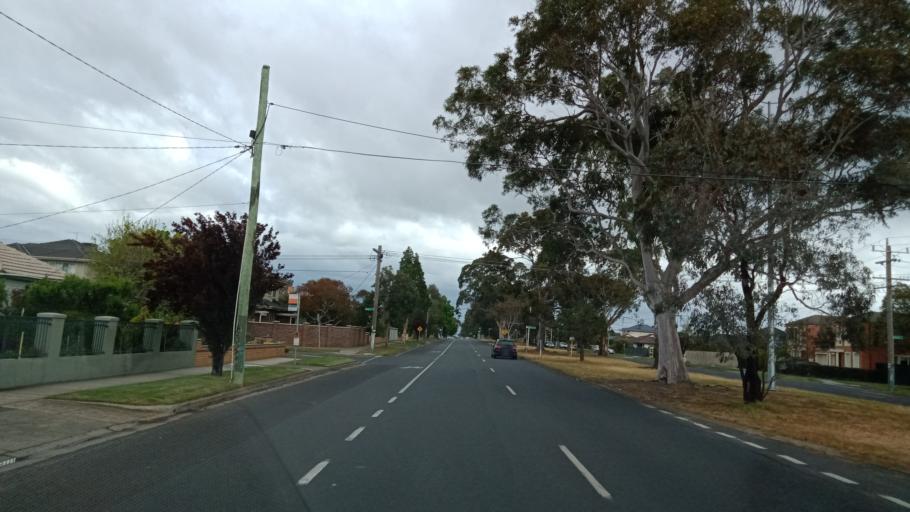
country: AU
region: Victoria
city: McKinnon
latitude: -37.9242
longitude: 145.0586
